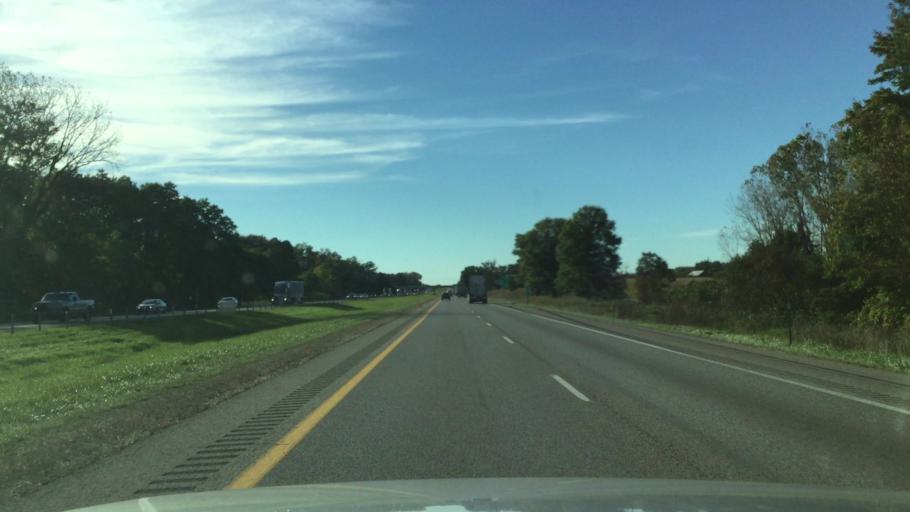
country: US
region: Michigan
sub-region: Calhoun County
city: Lakeview
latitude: 42.2677
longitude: -85.2691
